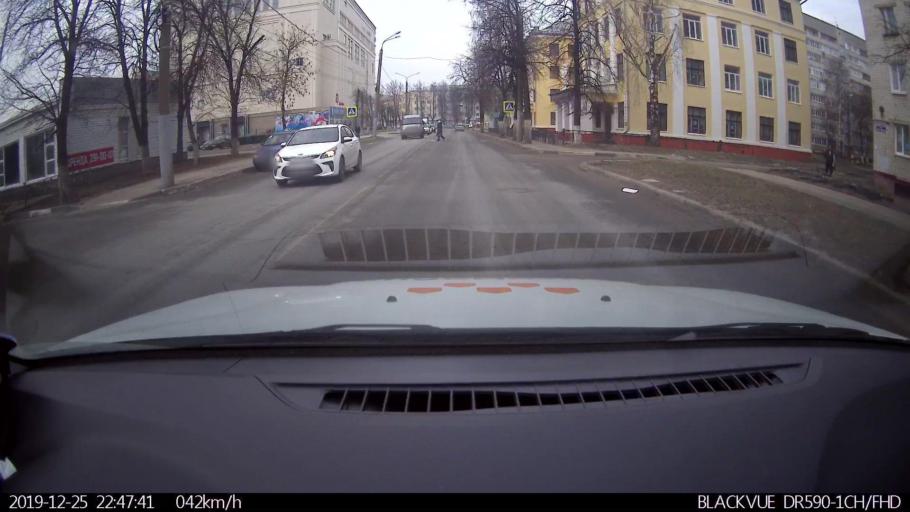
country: RU
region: Nizjnij Novgorod
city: Gorbatovka
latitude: 56.2416
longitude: 43.8679
